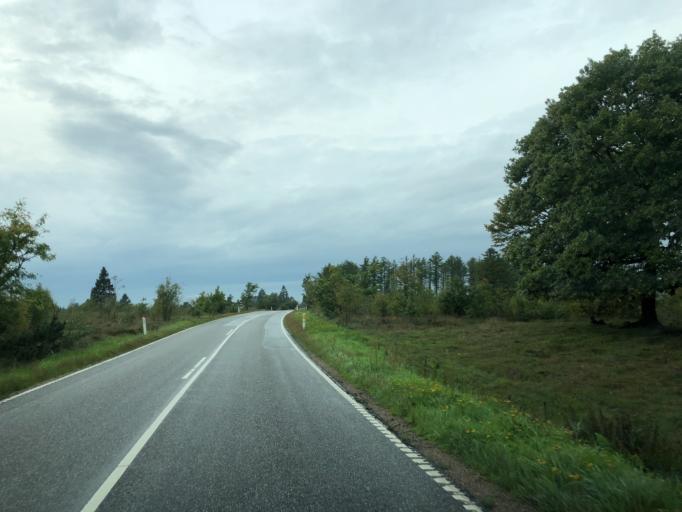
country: DK
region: Central Jutland
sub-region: Ikast-Brande Kommune
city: Brande
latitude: 55.9974
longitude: 9.1946
